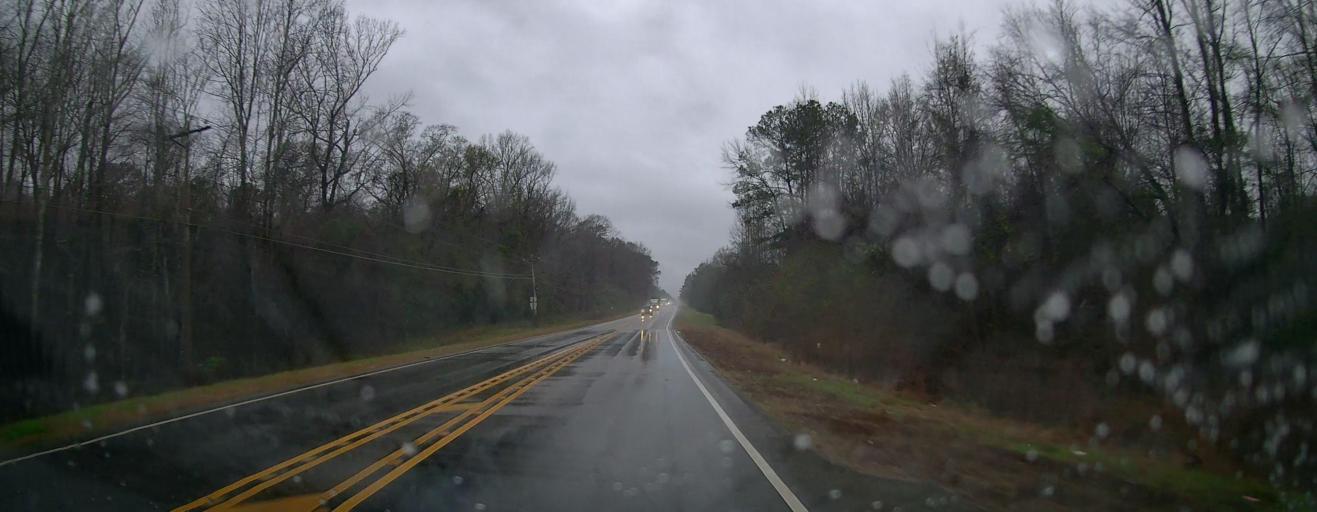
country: US
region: Alabama
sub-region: Autauga County
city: Prattville
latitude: 32.4755
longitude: -86.5231
